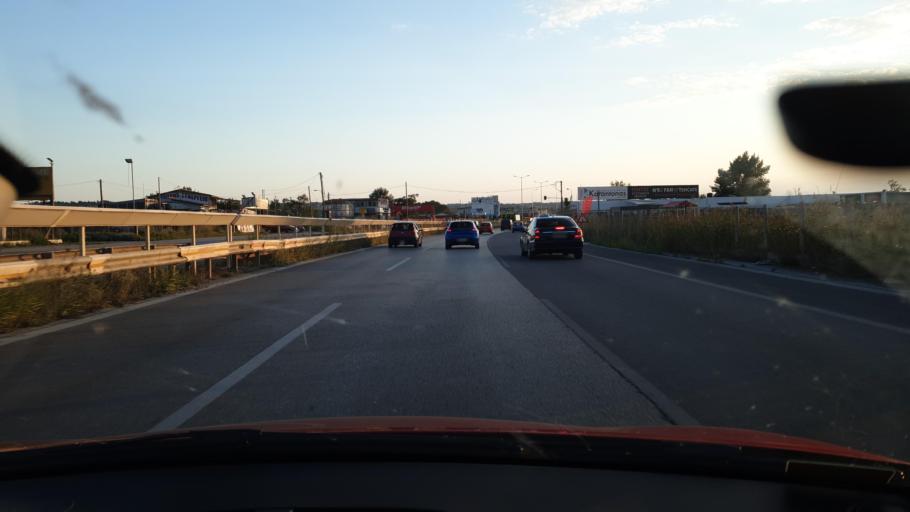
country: GR
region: Central Macedonia
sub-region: Nomos Thessalonikis
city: Neo Rysi
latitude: 40.5152
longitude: 22.9907
